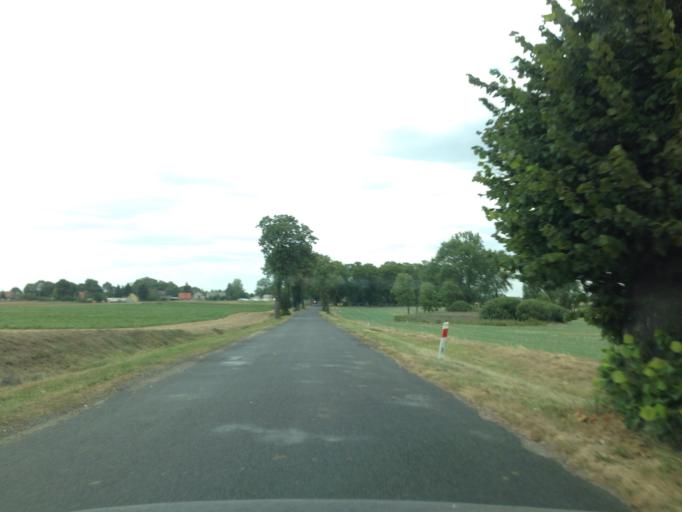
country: PL
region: Kujawsko-Pomorskie
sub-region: Powiat golubsko-dobrzynski
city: Kowalewo Pomorskie
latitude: 53.1923
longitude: 18.8274
